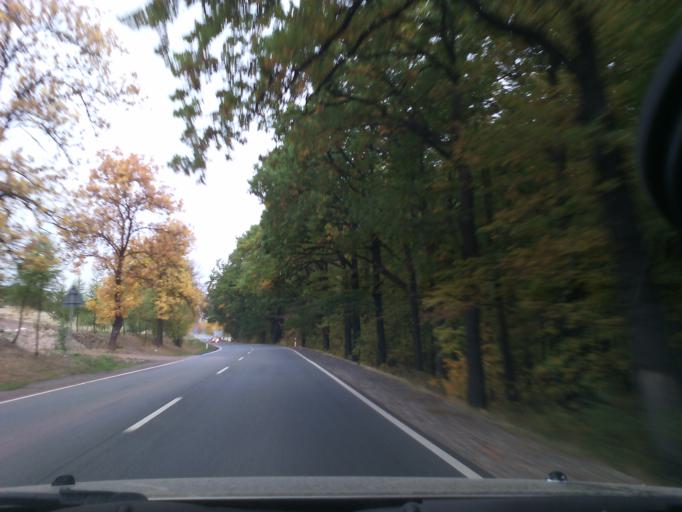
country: PL
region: Lower Silesian Voivodeship
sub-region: Powiat swidnicki
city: Swiebodzice
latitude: 50.8780
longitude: 16.2804
